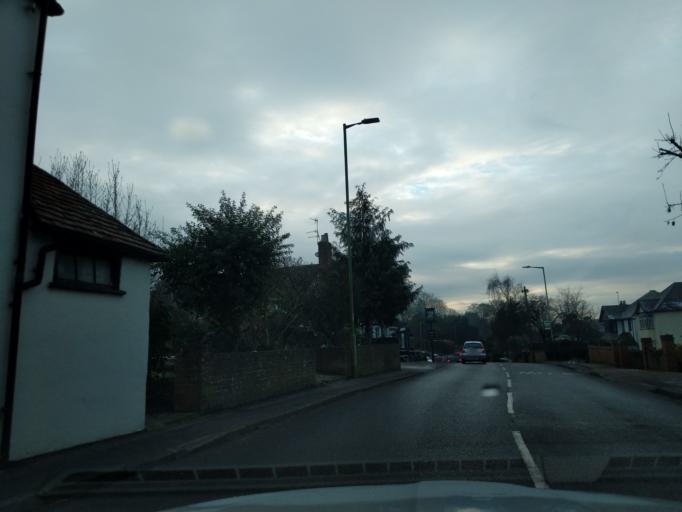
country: GB
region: England
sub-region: Hertfordshire
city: Abbots Langley
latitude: 51.7012
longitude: -0.4346
